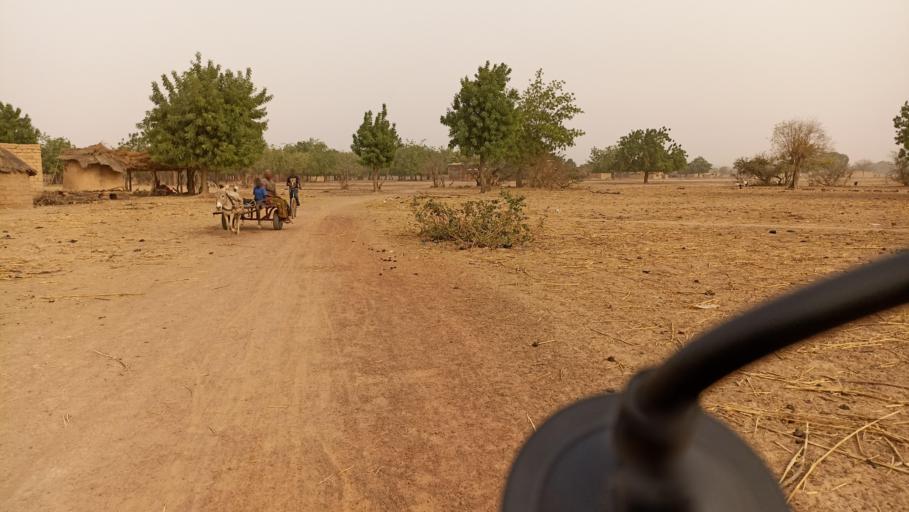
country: BF
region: Boucle du Mouhoun
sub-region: Province du Nayala
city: Toma
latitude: 12.8662
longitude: -2.7478
